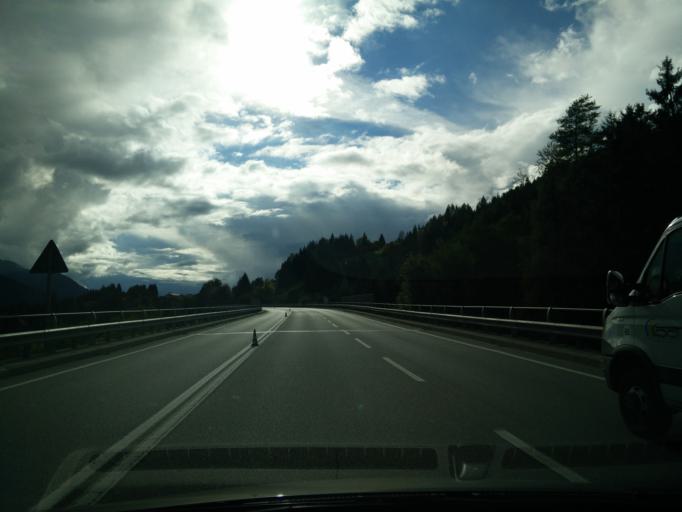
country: IT
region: Veneto
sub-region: Provincia di Belluno
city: Lozzo di Cadore
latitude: 46.4819
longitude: 12.4431
